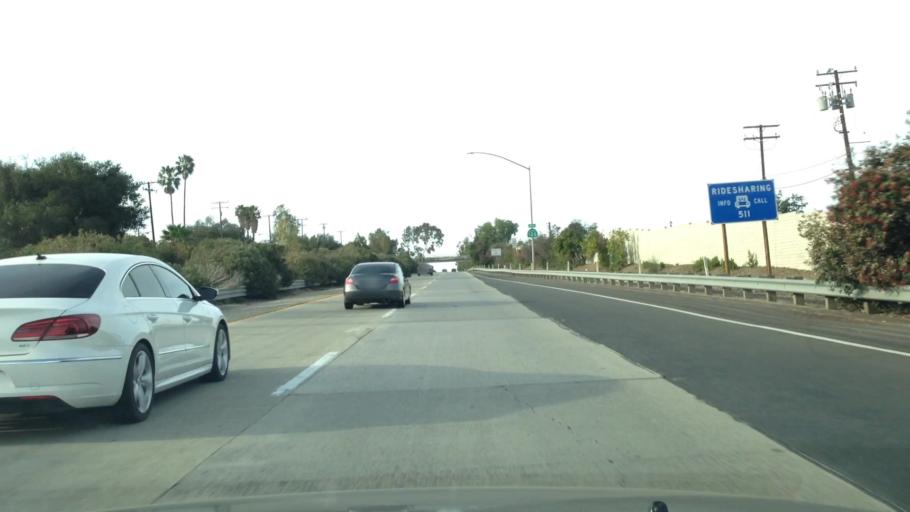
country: US
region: California
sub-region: Ventura County
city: Saticoy
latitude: 34.2872
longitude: -119.1607
